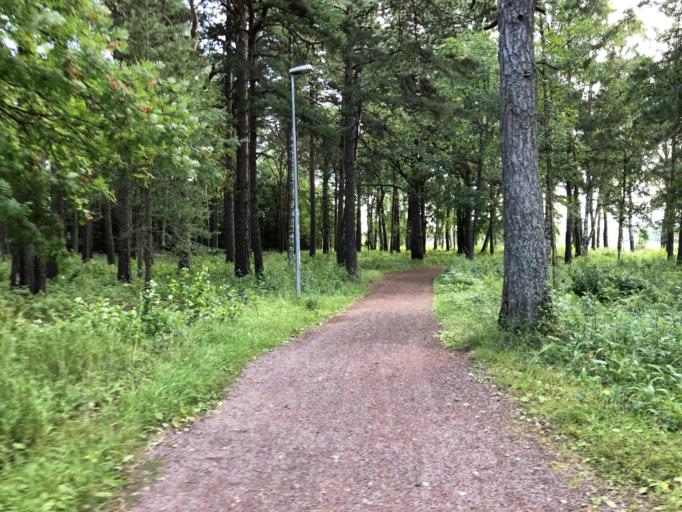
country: SE
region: Dalarna
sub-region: Mora Kommun
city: Mora
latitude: 61.0057
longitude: 14.5638
